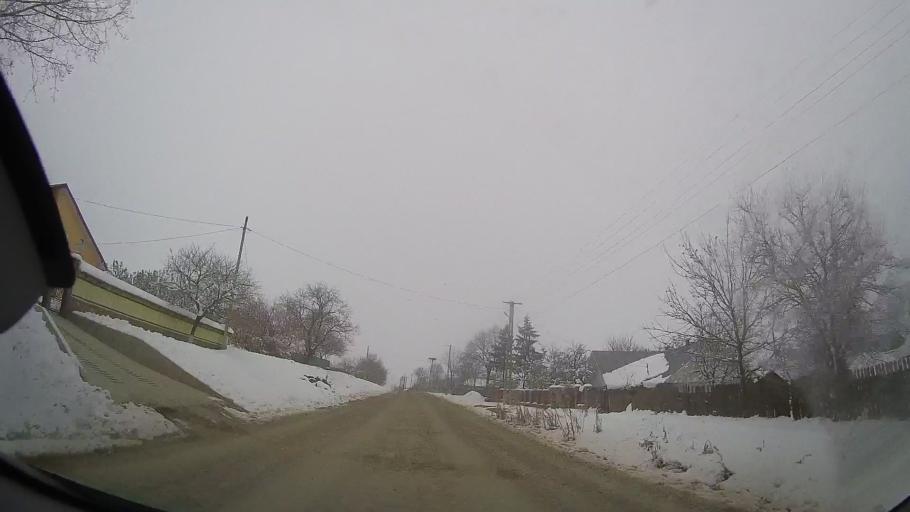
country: RO
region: Vaslui
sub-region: Comuna Todiresti
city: Todiresti
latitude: 46.8766
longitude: 27.3758
